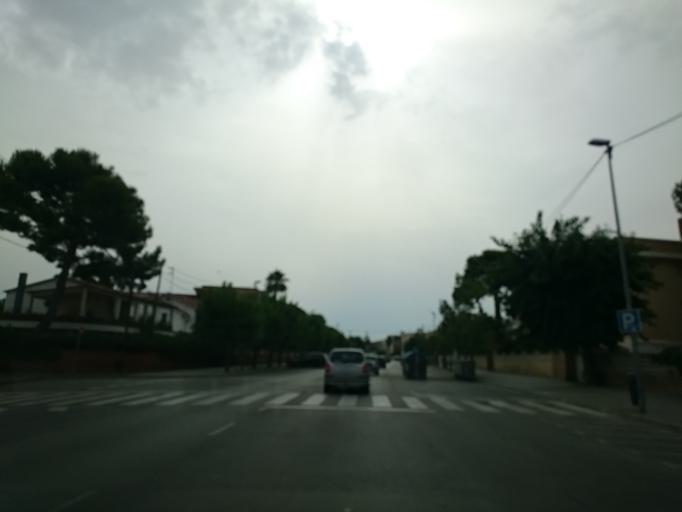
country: ES
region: Catalonia
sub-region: Provincia de Barcelona
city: Castelldefels
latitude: 41.2661
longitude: 1.9725
